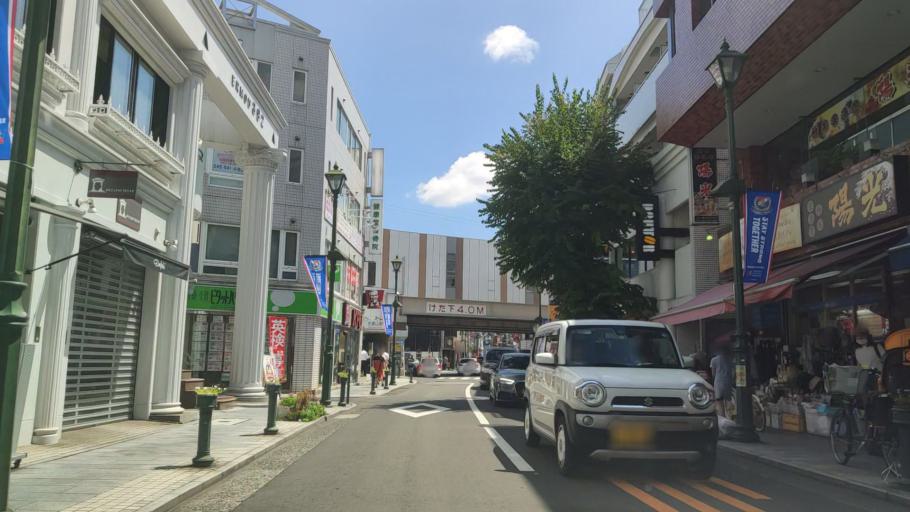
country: JP
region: Kanagawa
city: Yokohama
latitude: 35.5219
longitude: 139.6292
